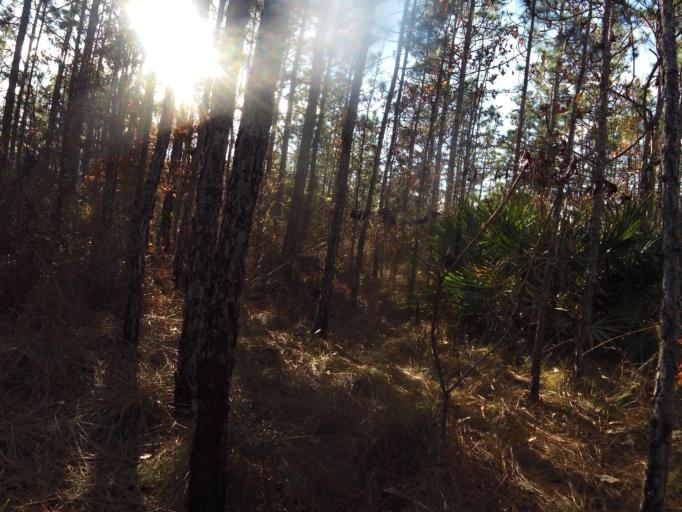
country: US
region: Florida
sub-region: Clay County
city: Middleburg
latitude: 30.1481
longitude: -81.9602
